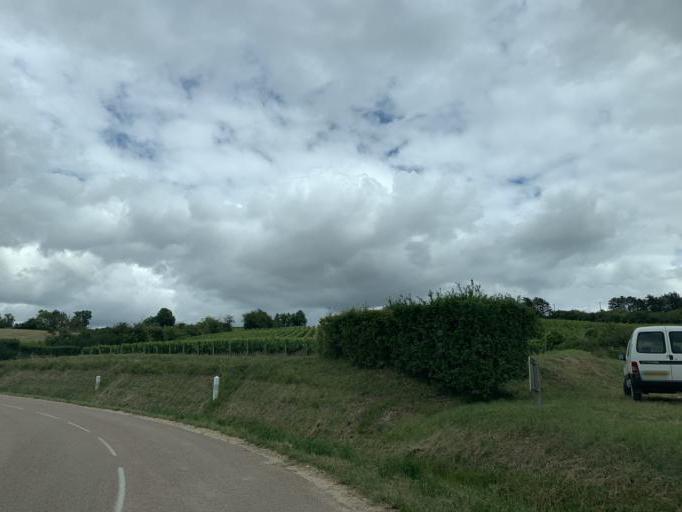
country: FR
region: Bourgogne
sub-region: Departement de l'Yonne
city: Saint-Bris-le-Vineux
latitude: 47.7144
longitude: 3.6769
